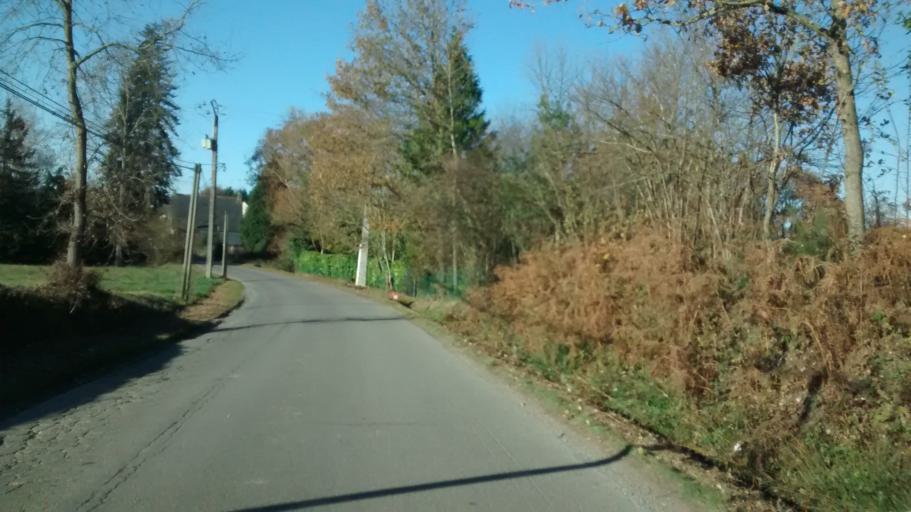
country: FR
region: Brittany
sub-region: Departement d'Ille-et-Vilaine
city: Liffre
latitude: 48.2037
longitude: -1.5077
